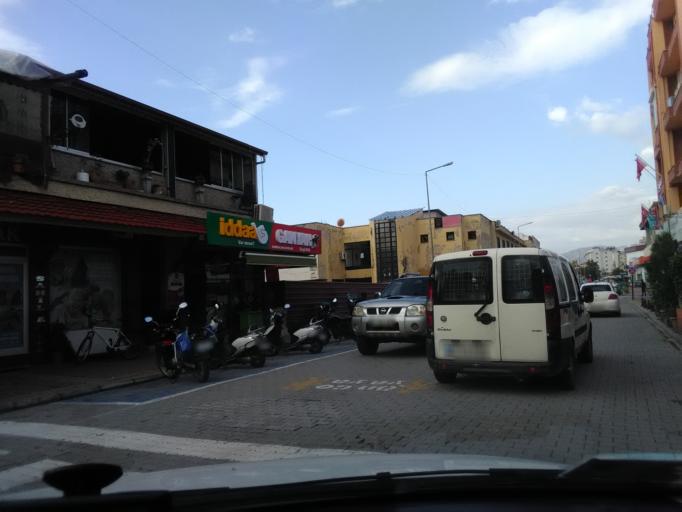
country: TR
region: Antalya
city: Gazipasa
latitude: 36.2684
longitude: 32.3176
